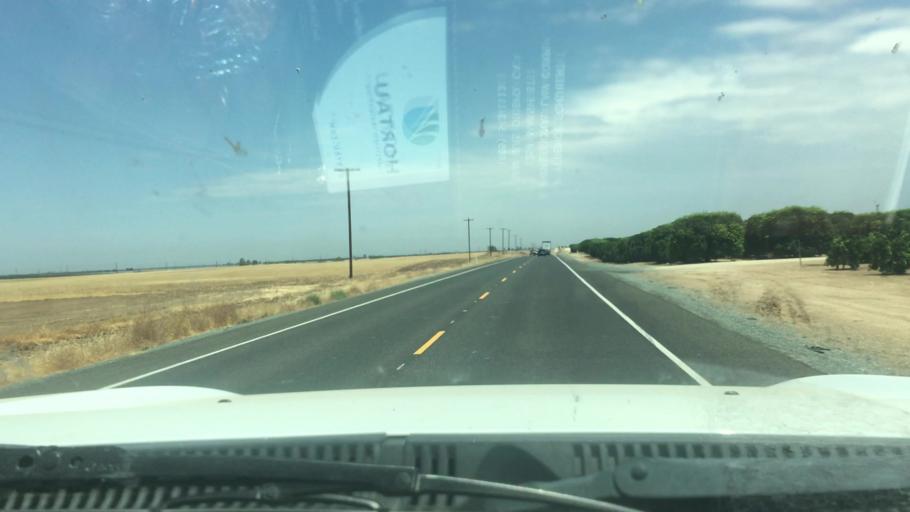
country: US
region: California
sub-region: Tulare County
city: Richgrove
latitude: 35.8228
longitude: -119.0536
